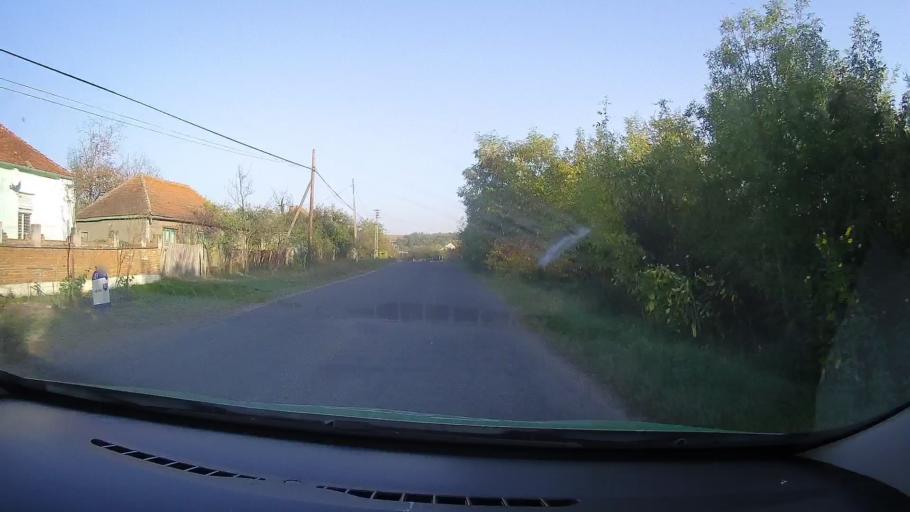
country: RO
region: Arad
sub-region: Comuna Silindia
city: Silindia
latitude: 46.3360
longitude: 21.9271
